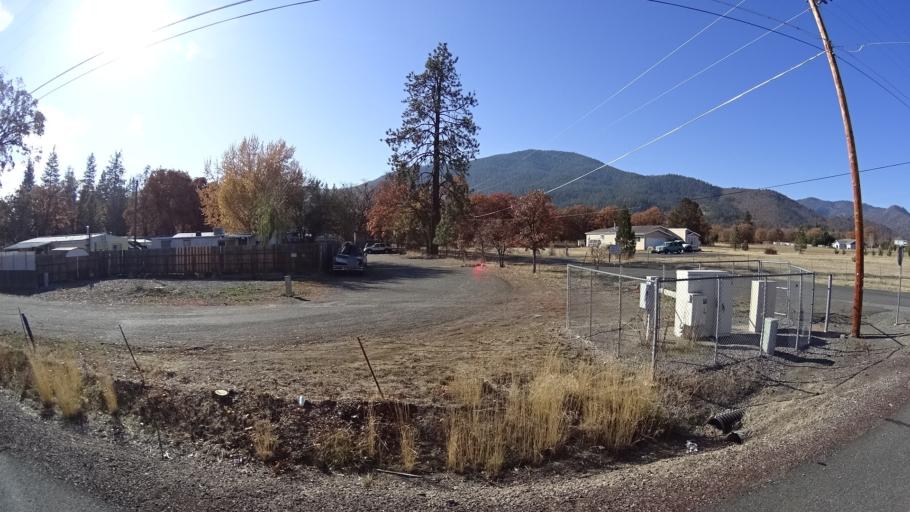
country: US
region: California
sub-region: Siskiyou County
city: Yreka
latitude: 41.6594
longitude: -122.5926
